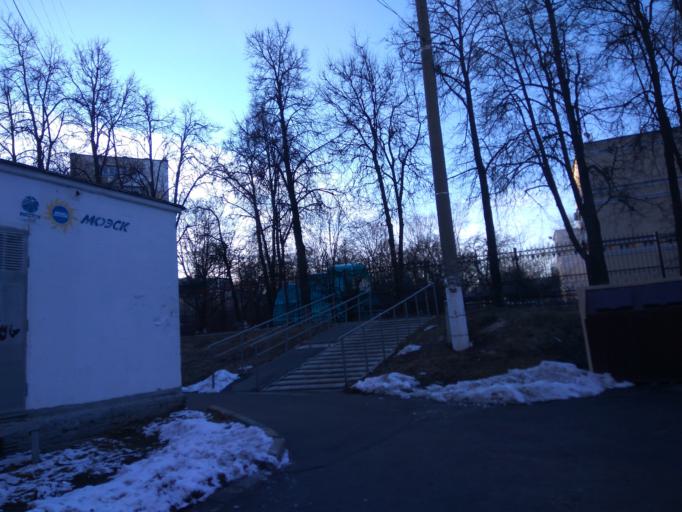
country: RU
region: Moscow
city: Tsaritsyno
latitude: 55.6221
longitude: 37.6639
